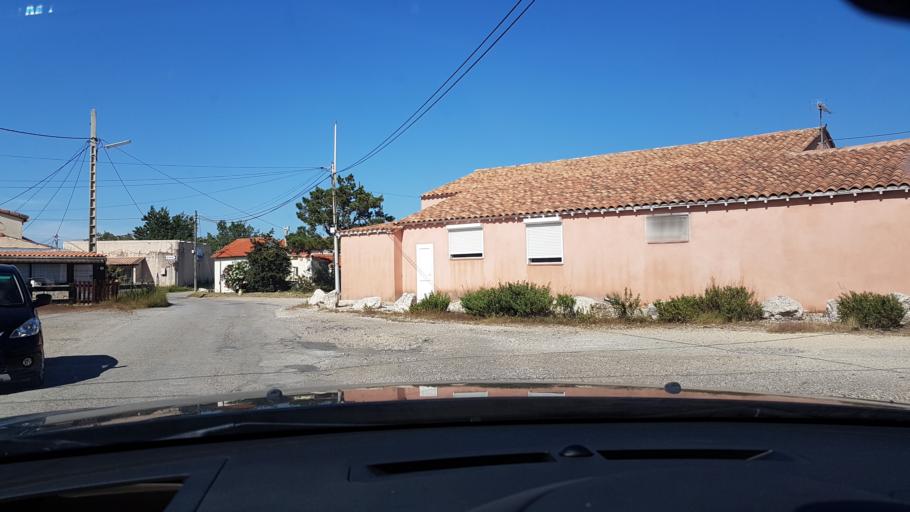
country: FR
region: Provence-Alpes-Cote d'Azur
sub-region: Departement des Bouches-du-Rhone
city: Port-Saint-Louis-du-Rhone
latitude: 43.3896
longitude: 4.8510
